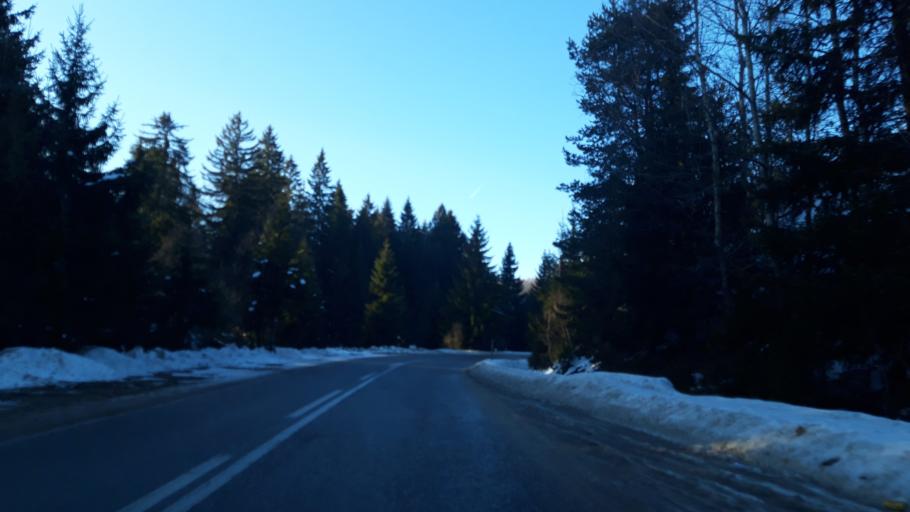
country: BA
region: Republika Srpska
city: Han Pijesak
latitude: 44.1224
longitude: 18.9658
